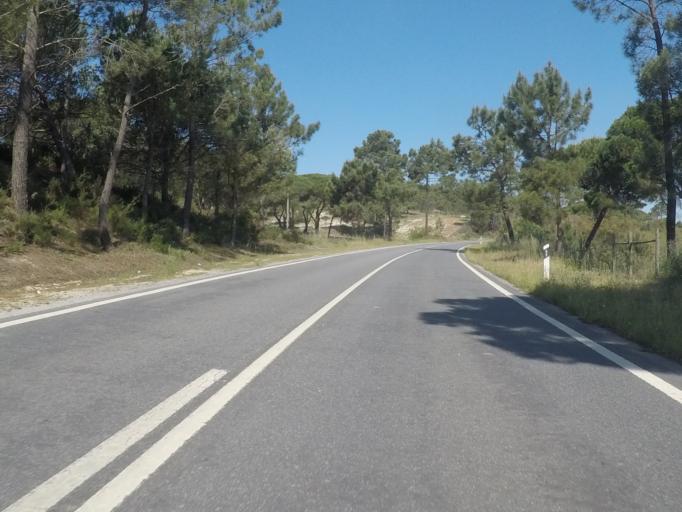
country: PT
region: Setubal
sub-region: Grandola
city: Grandola
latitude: 38.3015
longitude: -8.7333
